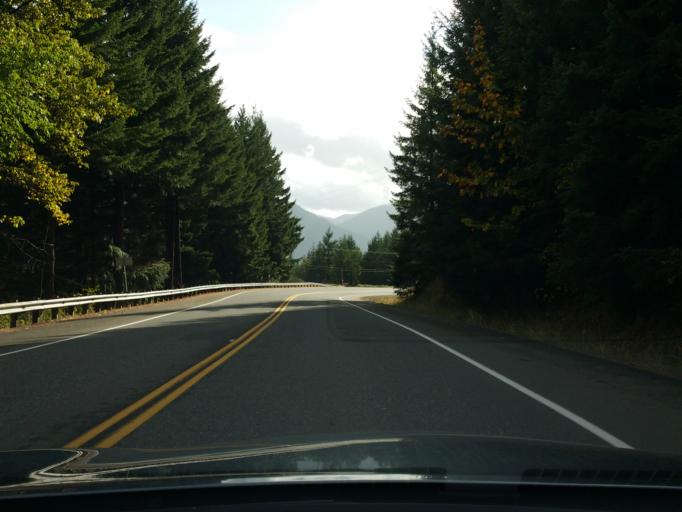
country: US
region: Washington
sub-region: Skamania County
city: Carson
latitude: 45.7210
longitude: -121.8206
